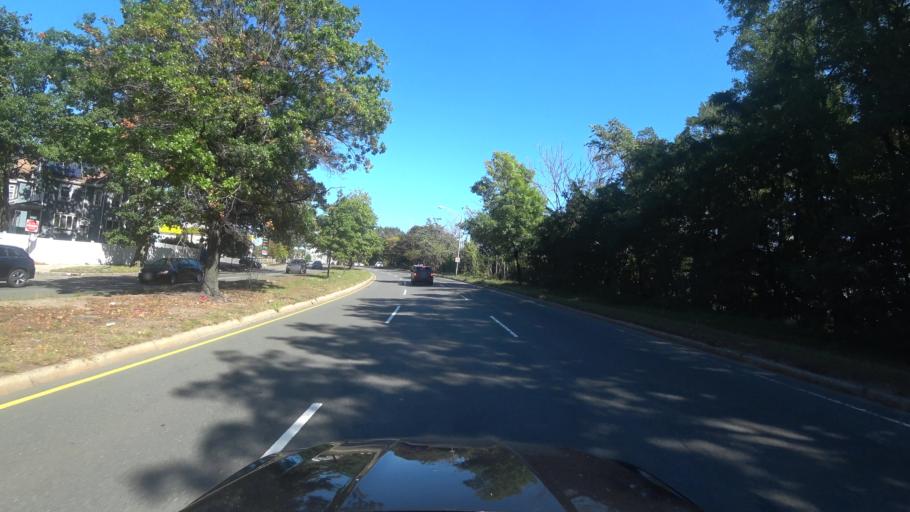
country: US
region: Massachusetts
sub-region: Suffolk County
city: Revere
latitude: 42.4028
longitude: -71.0105
